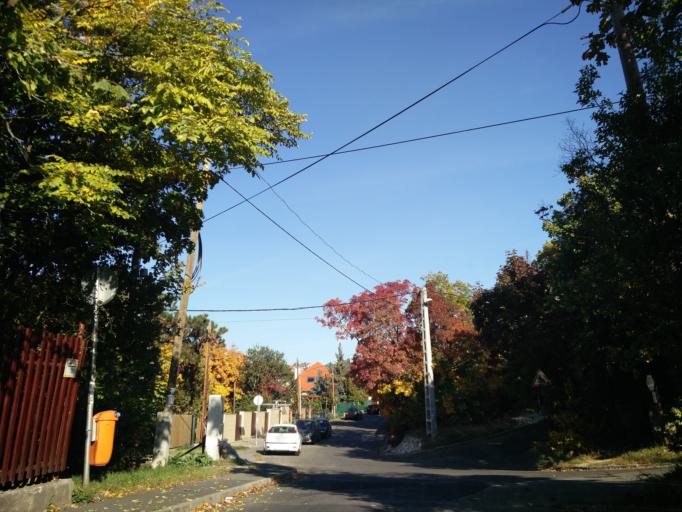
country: HU
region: Budapest
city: Budapest II. keruelet
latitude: 47.5258
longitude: 18.9974
